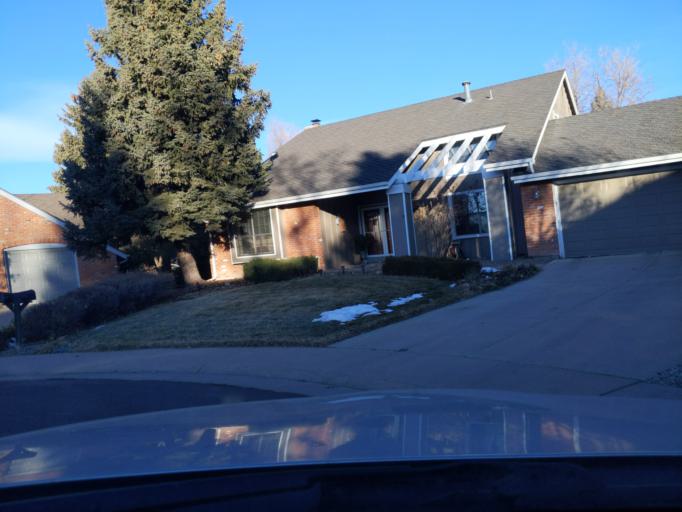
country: US
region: Colorado
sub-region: Douglas County
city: Acres Green
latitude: 39.5703
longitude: -104.8903
